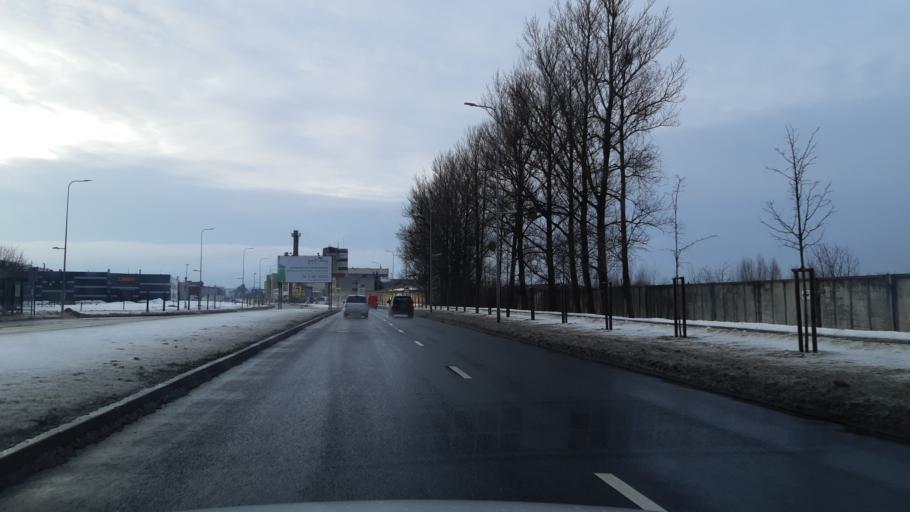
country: LT
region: Kauno apskritis
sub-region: Kaunas
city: Aleksotas
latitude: 54.8753
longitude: 23.9058
